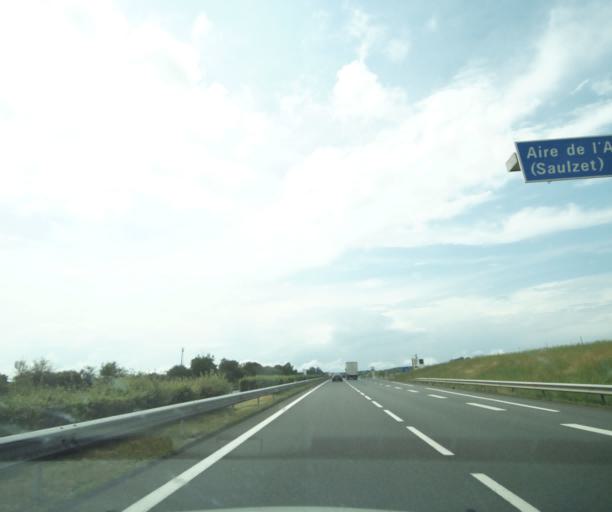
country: FR
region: Auvergne
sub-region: Departement de l'Allier
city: Doyet
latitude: 46.3536
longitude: 2.8108
